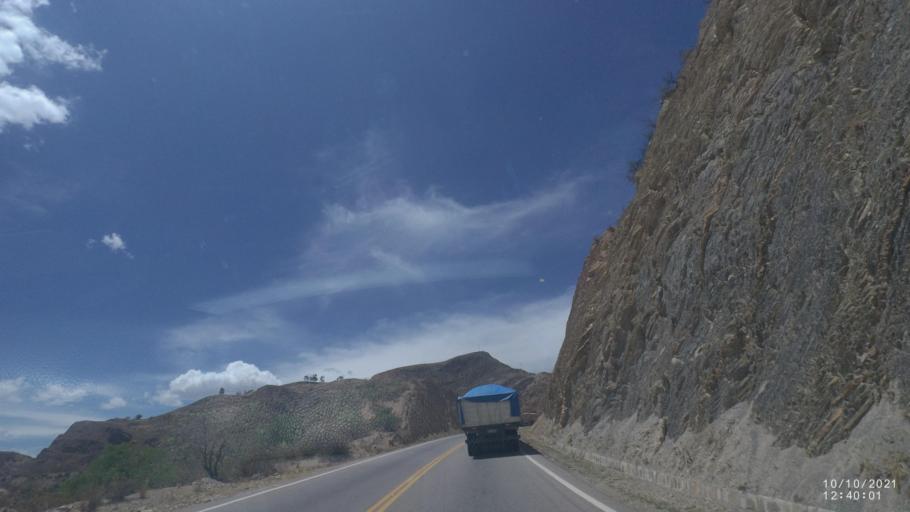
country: BO
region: Cochabamba
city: Irpa Irpa
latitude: -17.6422
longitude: -66.3915
